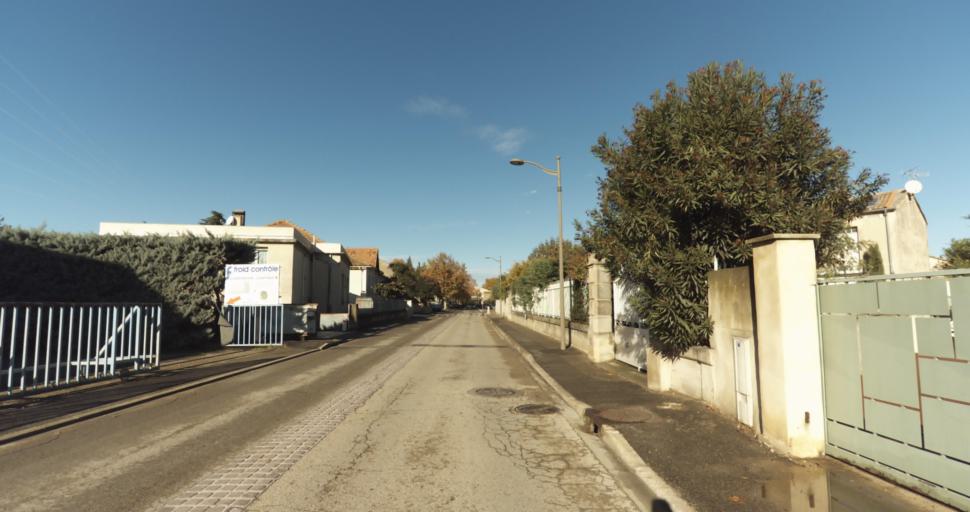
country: FR
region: Provence-Alpes-Cote d'Azur
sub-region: Departement des Bouches-du-Rhone
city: Rognonas
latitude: 43.8968
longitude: 4.8054
